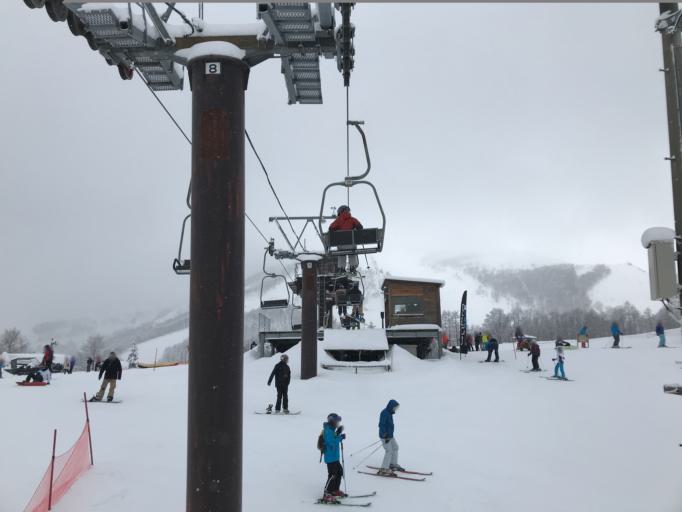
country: JP
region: Nagano
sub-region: Kitaazumi Gun
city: Hakuba
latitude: 36.7103
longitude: 137.8193
